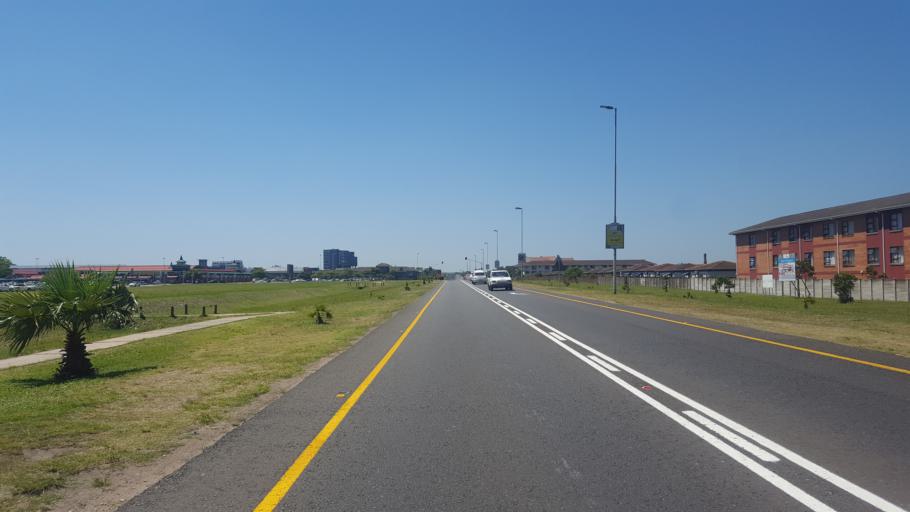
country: ZA
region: KwaZulu-Natal
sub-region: uThungulu District Municipality
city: Richards Bay
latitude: -28.7577
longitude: 32.0521
